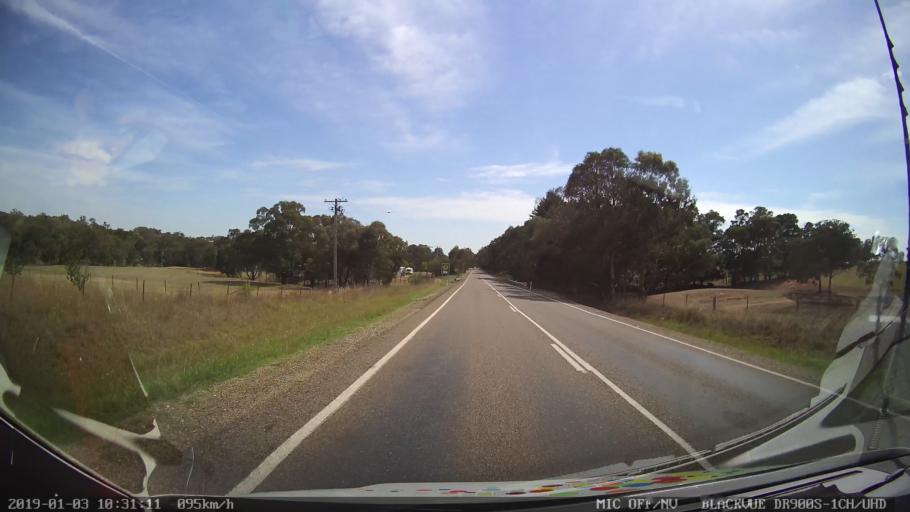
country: AU
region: New South Wales
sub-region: Young
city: Young
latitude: -34.3532
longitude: 148.2747
